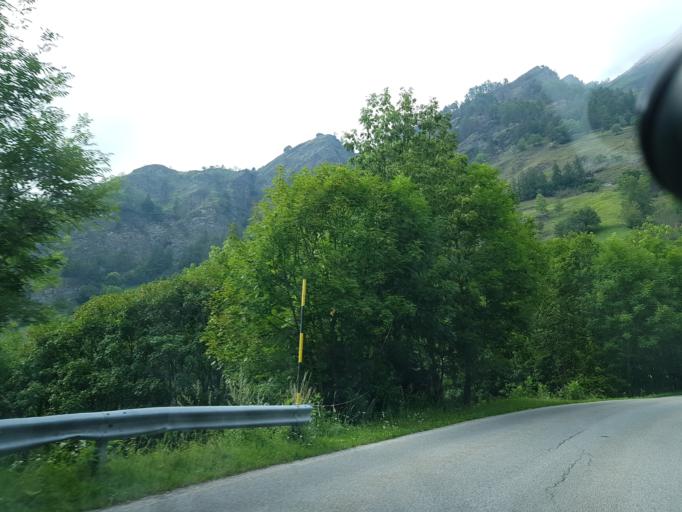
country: IT
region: Piedmont
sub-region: Provincia di Cuneo
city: Casteldelfino
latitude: 44.5864
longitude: 7.0451
